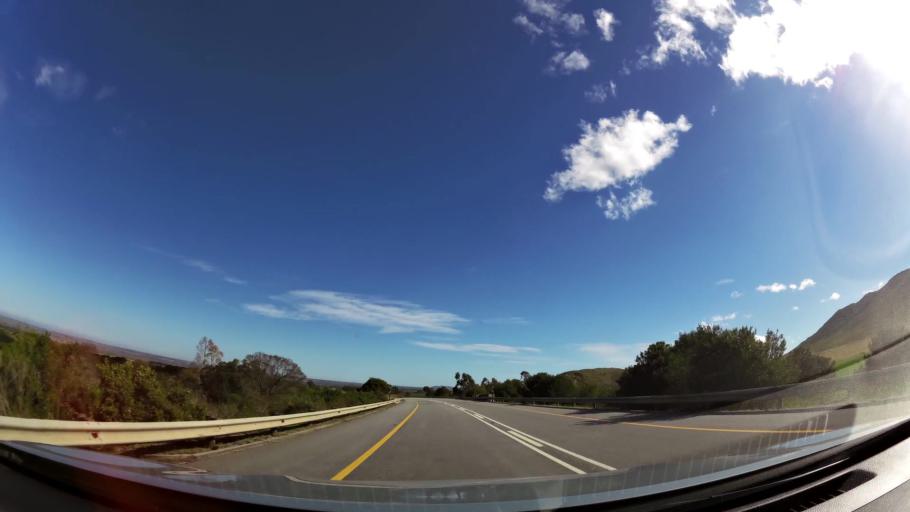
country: ZA
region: Eastern Cape
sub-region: Cacadu District Municipality
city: Kruisfontein
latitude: -33.9944
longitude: 24.6937
